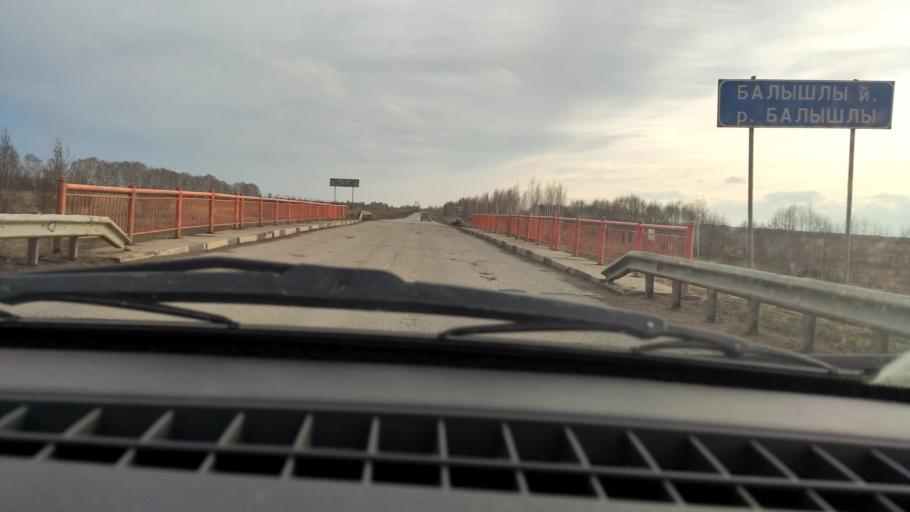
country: RU
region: Bashkortostan
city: Chishmy
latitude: 54.4416
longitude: 55.2404
